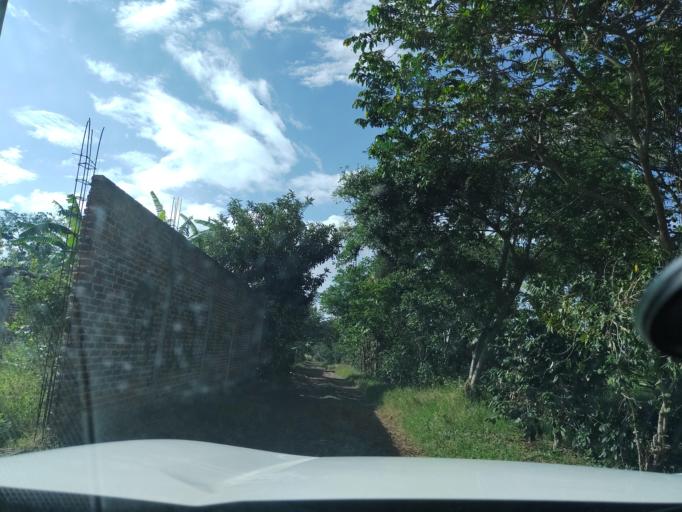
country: MX
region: Veracruz
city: Coatepec
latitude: 19.4806
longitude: -96.9354
